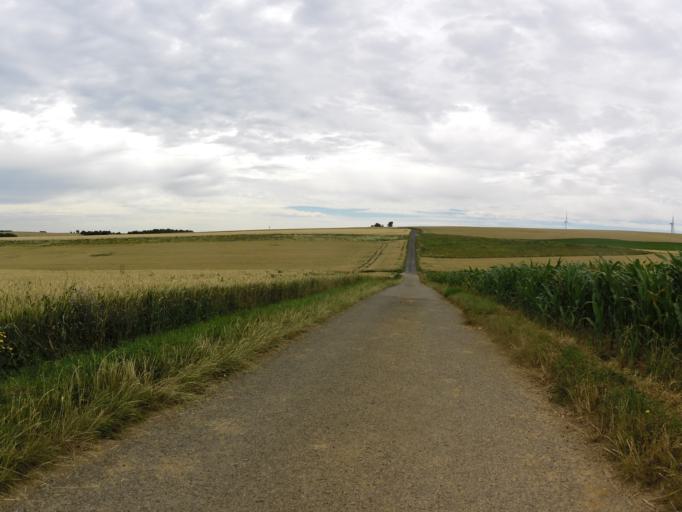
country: DE
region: Bavaria
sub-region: Regierungsbezirk Unterfranken
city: Reichenberg
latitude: 49.7129
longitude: 9.9017
